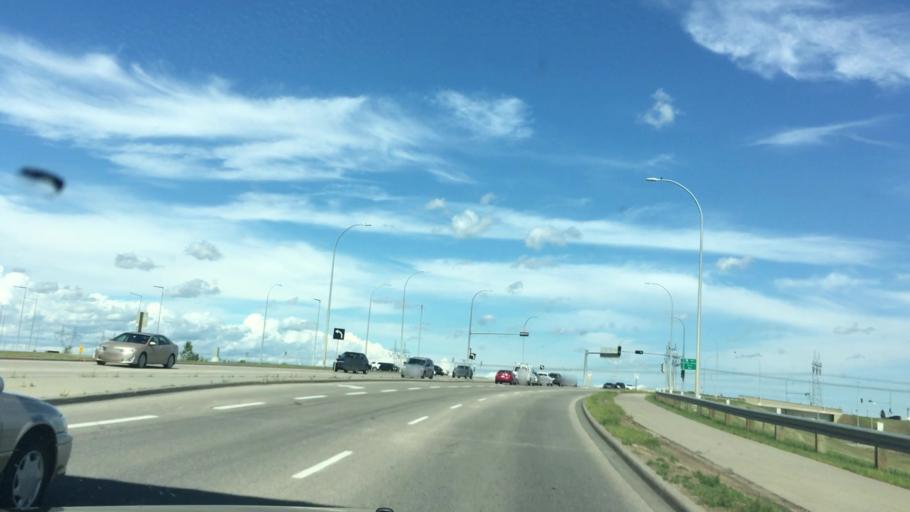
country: CA
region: Alberta
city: Edmonton
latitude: 53.4321
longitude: -113.5182
